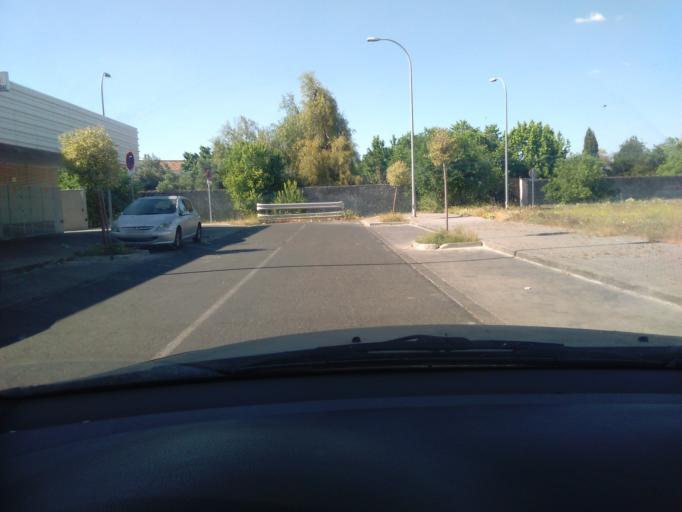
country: ES
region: Andalusia
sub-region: Provincia de Sevilla
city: Sevilla
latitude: 37.3870
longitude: -5.9139
